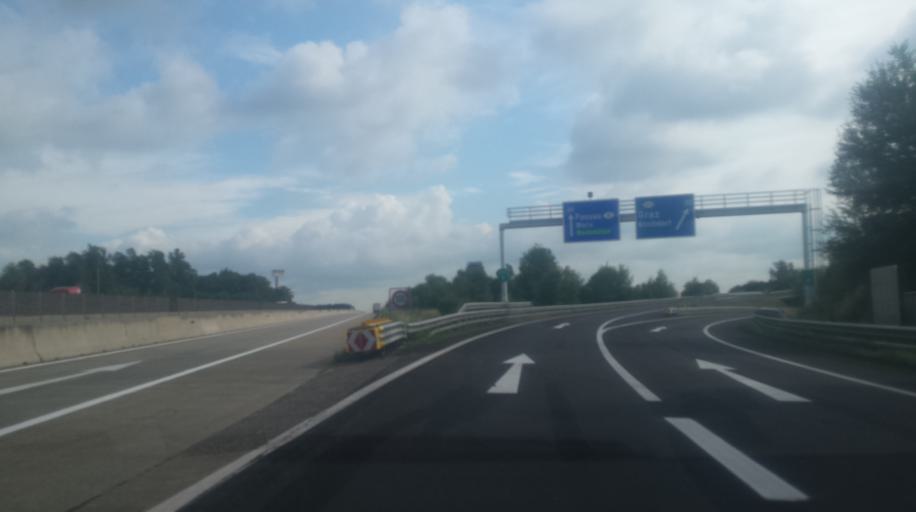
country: AT
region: Upper Austria
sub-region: Wels-Land
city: Sattledt
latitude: 48.0601
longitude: 14.0355
